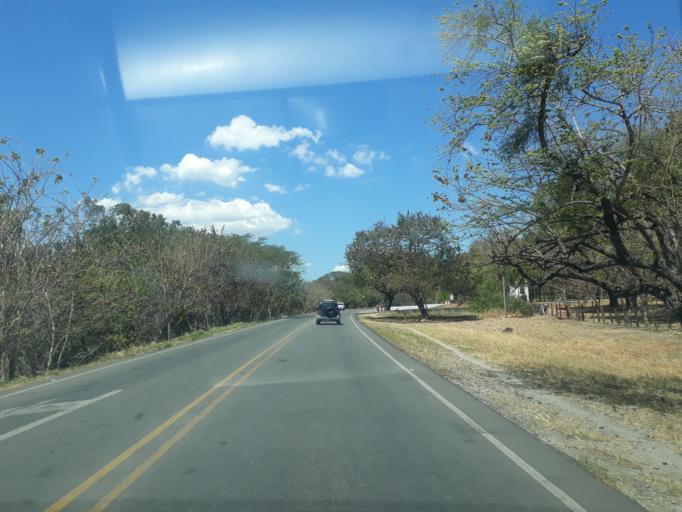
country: CR
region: Guanacaste
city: Liberia
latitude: 10.6483
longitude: -85.4612
